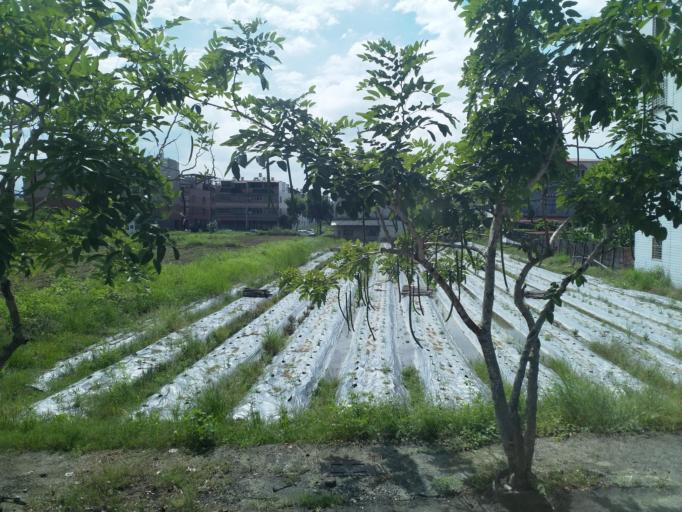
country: TW
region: Taiwan
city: Yujing
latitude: 22.9032
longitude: 120.5448
